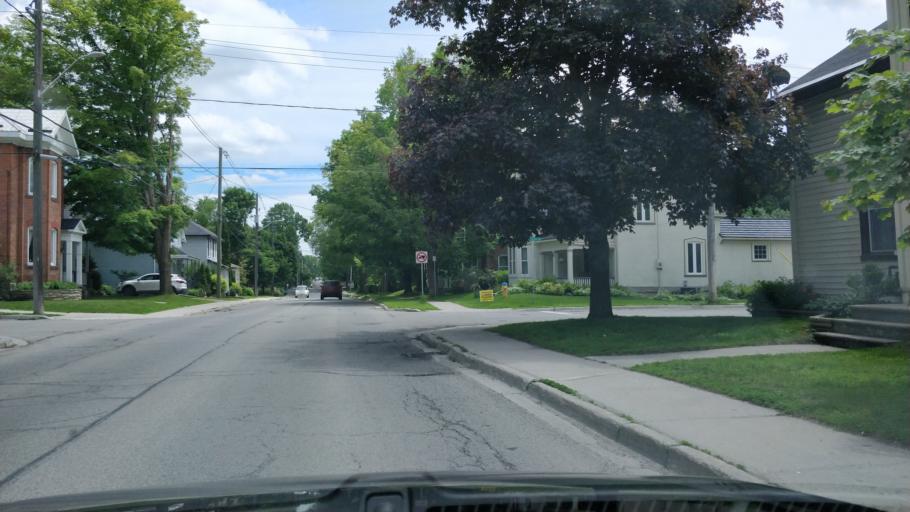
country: CA
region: Ontario
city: Perth
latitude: 44.9038
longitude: -76.2517
